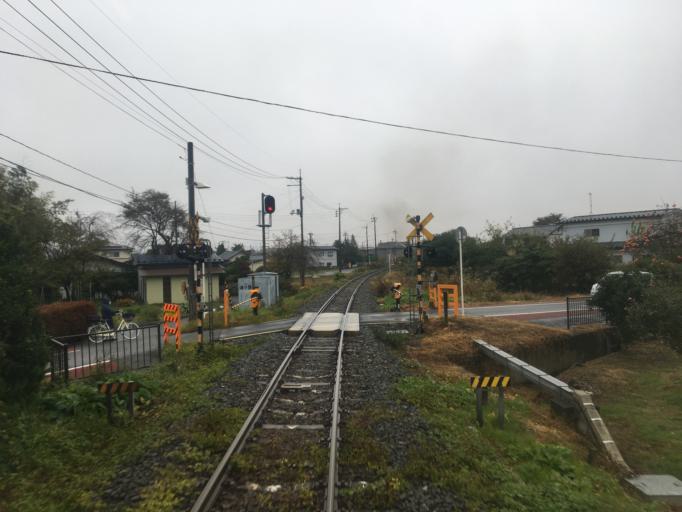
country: JP
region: Miyagi
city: Furukawa
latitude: 38.6559
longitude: 140.8684
